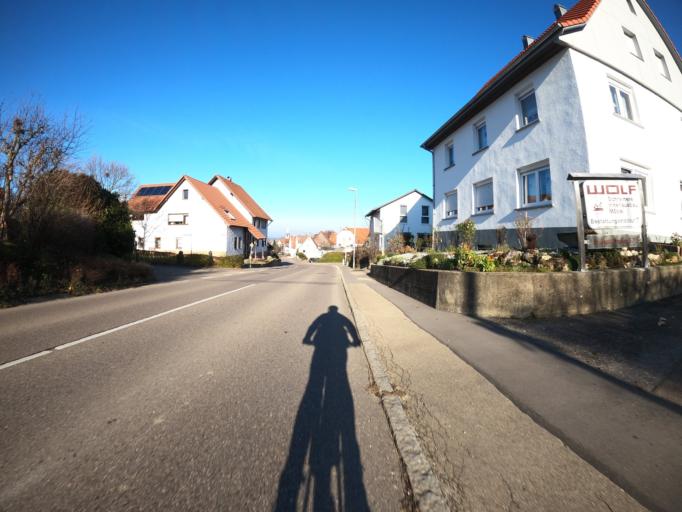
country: DE
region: Baden-Wuerttemberg
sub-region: Regierungsbezirk Stuttgart
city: Gammelshausen
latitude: 48.6375
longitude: 9.6505
